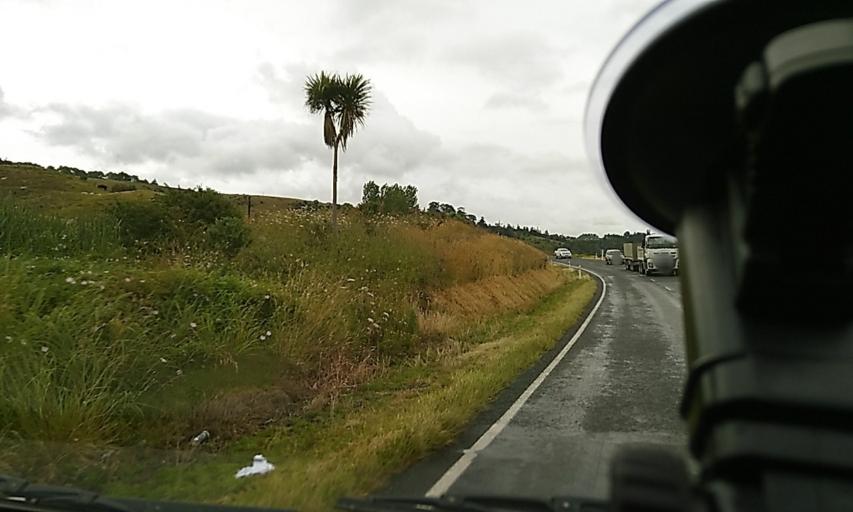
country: NZ
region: Auckland
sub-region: Auckland
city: Pukekohe East
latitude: -37.3162
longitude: 174.9540
